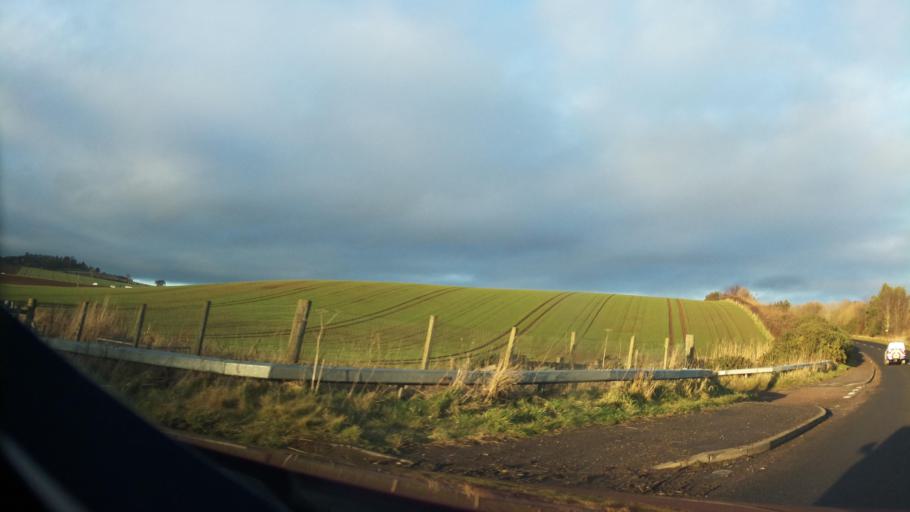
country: GB
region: Scotland
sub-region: Fife
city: Tayport
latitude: 56.4903
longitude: -2.8051
